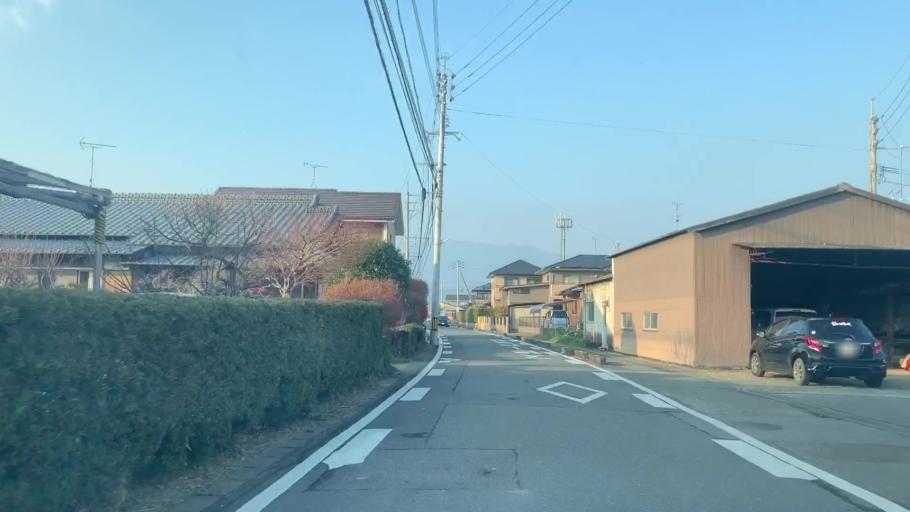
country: JP
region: Saga Prefecture
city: Saga-shi
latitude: 33.2709
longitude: 130.2293
